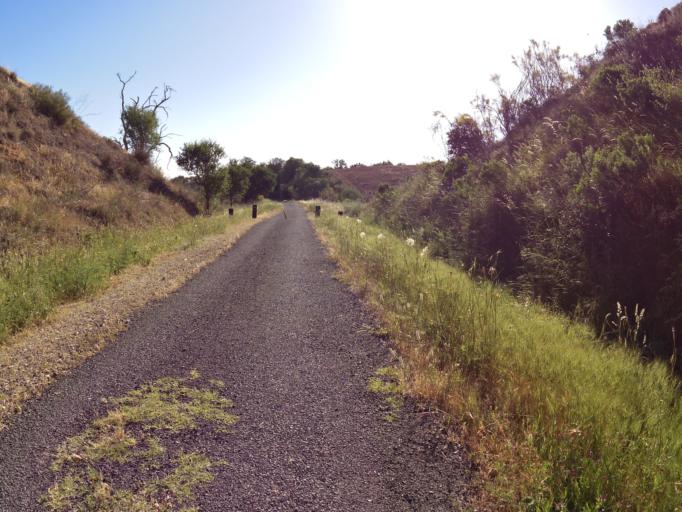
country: ES
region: Andalusia
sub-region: Province of Cordoba
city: Luque
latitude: 37.5664
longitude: -4.2380
